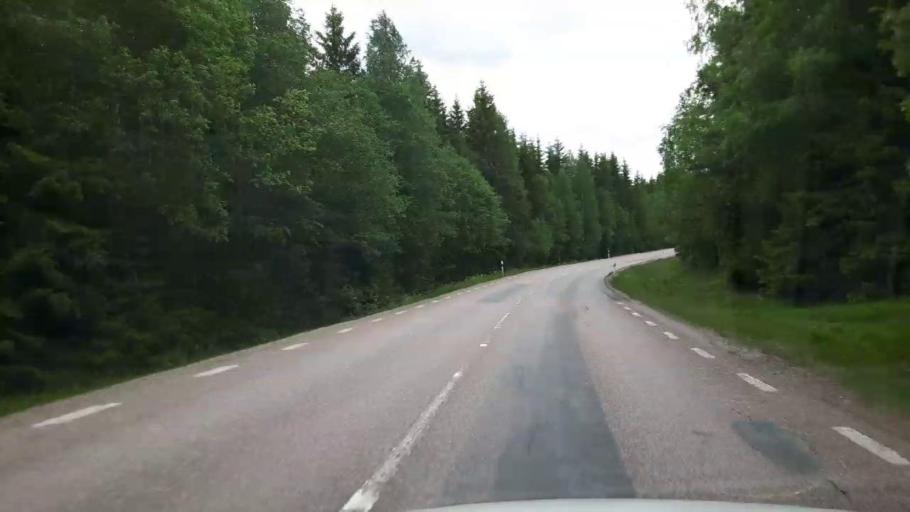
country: SE
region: Dalarna
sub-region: Hedemora Kommun
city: Brunna
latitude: 60.1853
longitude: 15.9994
